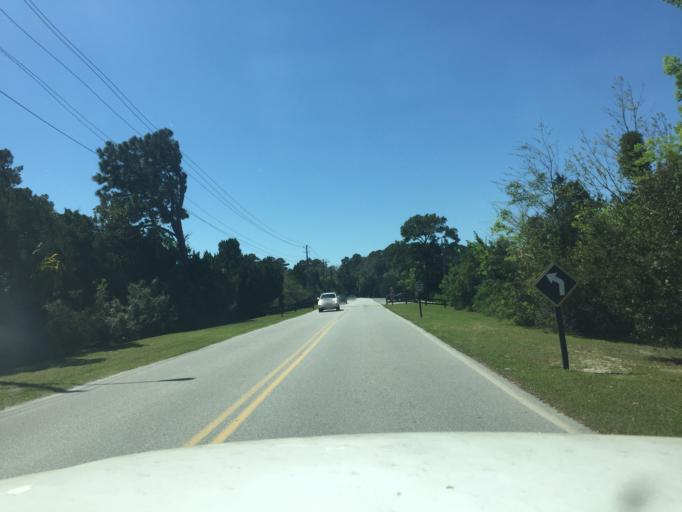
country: US
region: Georgia
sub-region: Chatham County
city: Isle of Hope
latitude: 32.0016
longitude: -81.0466
